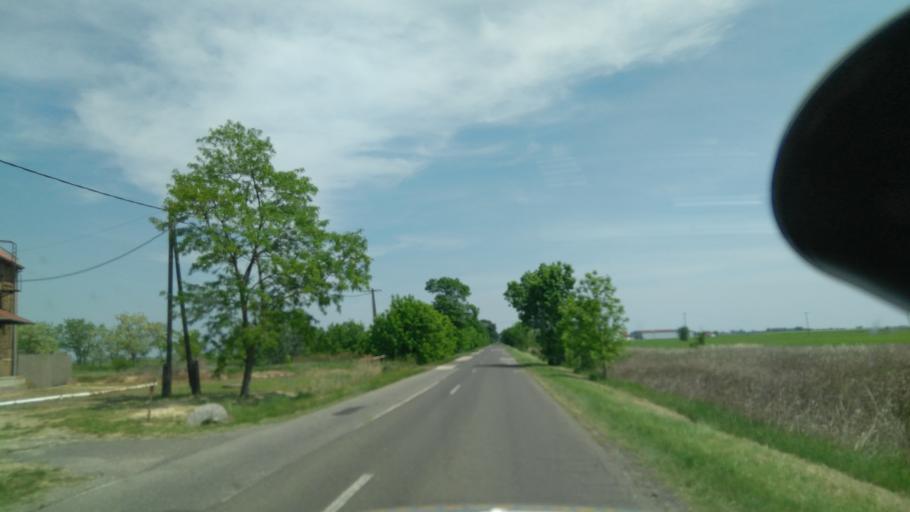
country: HU
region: Csongrad
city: Szekkutas
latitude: 46.5717
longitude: 20.5508
